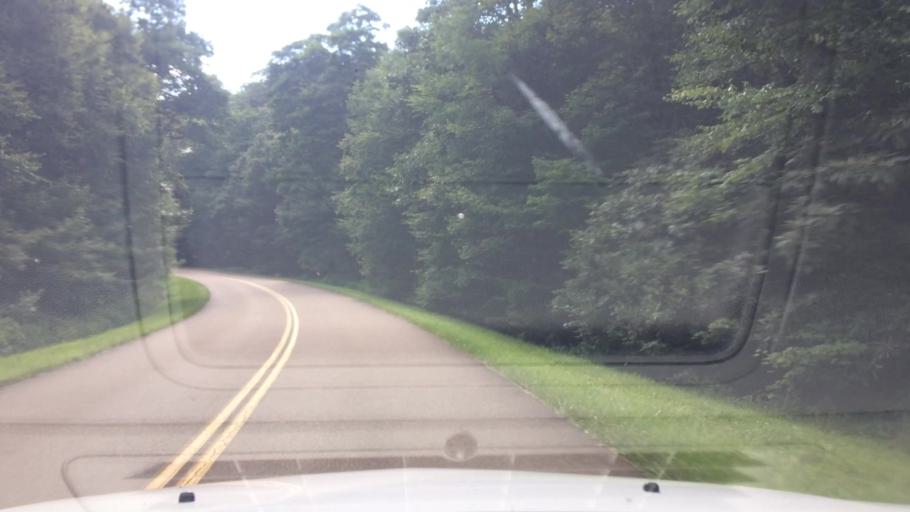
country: US
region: North Carolina
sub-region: Watauga County
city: Blowing Rock
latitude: 36.1563
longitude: -81.6776
